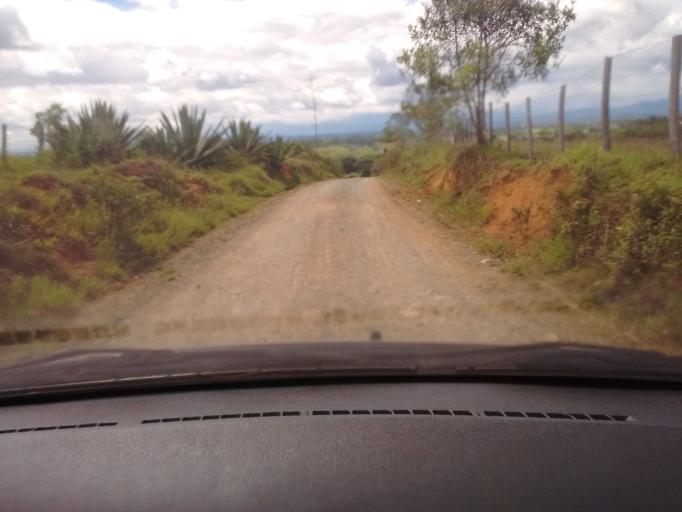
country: CO
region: Cauca
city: El Tambo
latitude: 2.4552
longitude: -76.8243
